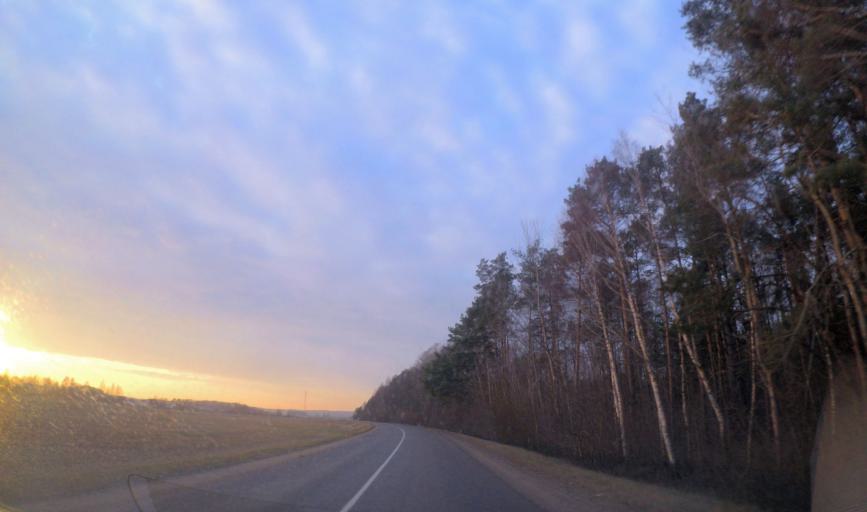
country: BY
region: Grodnenskaya
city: Hrodna
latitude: 53.7633
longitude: 23.9513
